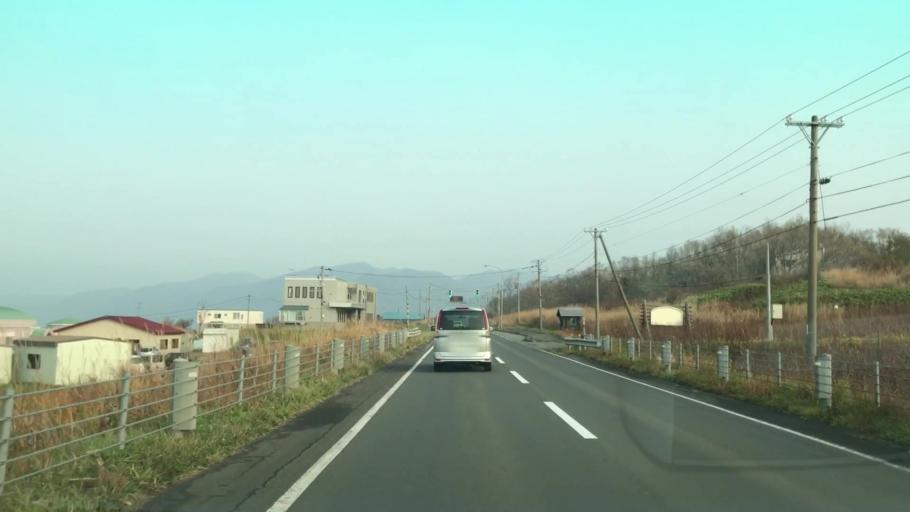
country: JP
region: Hokkaido
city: Ishikari
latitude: 43.3747
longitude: 141.4275
